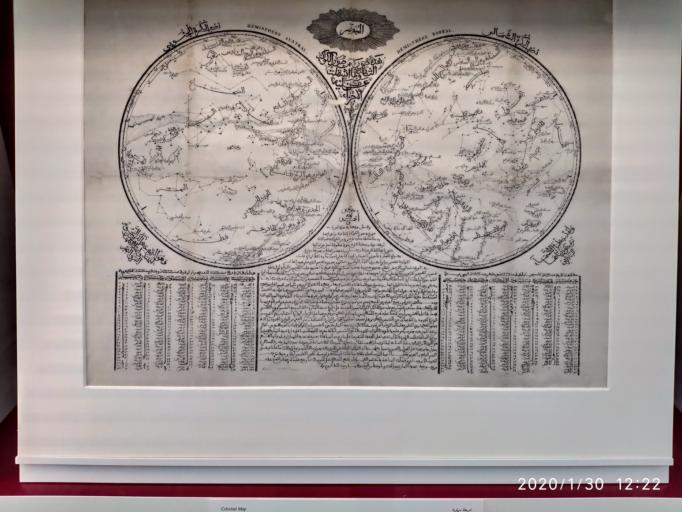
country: QA
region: Baladiyat ar Rayyan
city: Ar Rayyan
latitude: 25.3179
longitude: 51.4415
